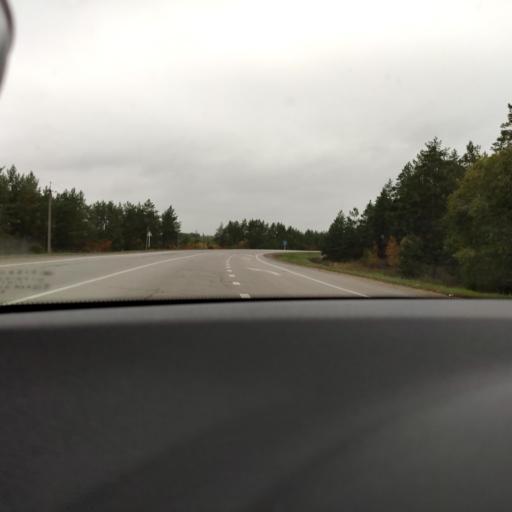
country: RU
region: Samara
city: Mirnyy
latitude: 53.5292
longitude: 50.3070
